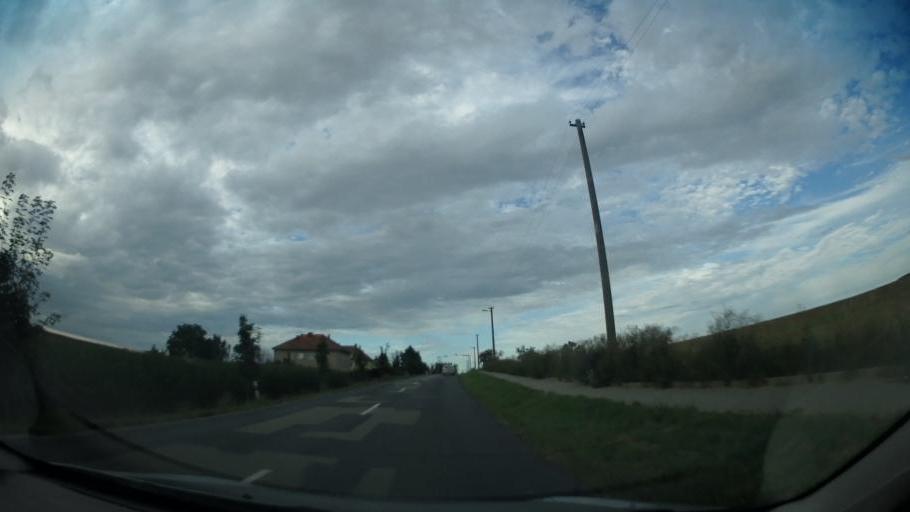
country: CZ
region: South Moravian
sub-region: Okres Blansko
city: Boskovice
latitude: 49.4967
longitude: 16.6639
